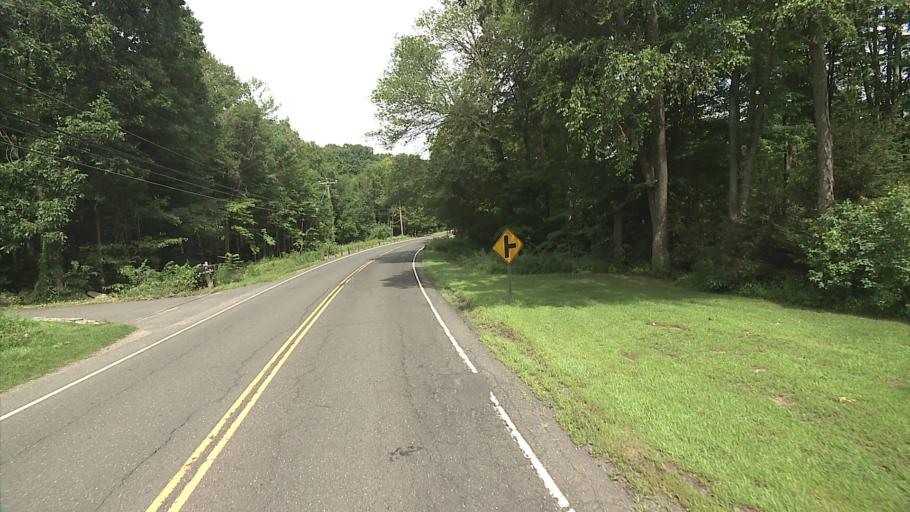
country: US
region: Connecticut
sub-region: New Haven County
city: Oxford
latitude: 41.4568
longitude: -73.1510
